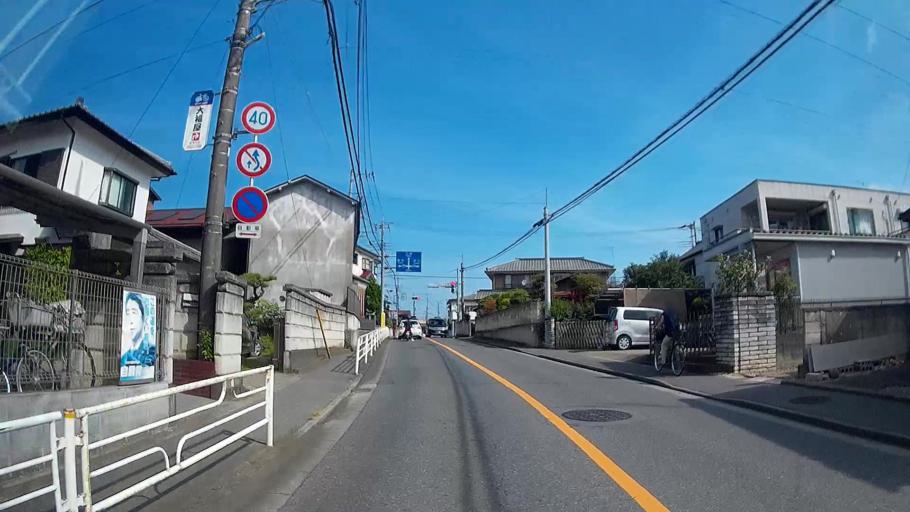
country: JP
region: Saitama
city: Hanno
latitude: 35.8430
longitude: 139.3560
